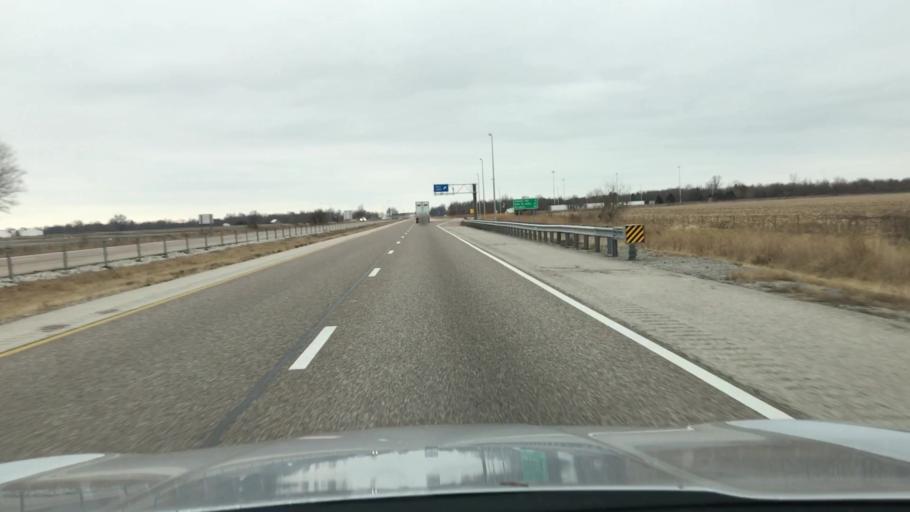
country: US
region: Illinois
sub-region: Madison County
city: Worden
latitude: 38.8774
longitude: -89.8464
